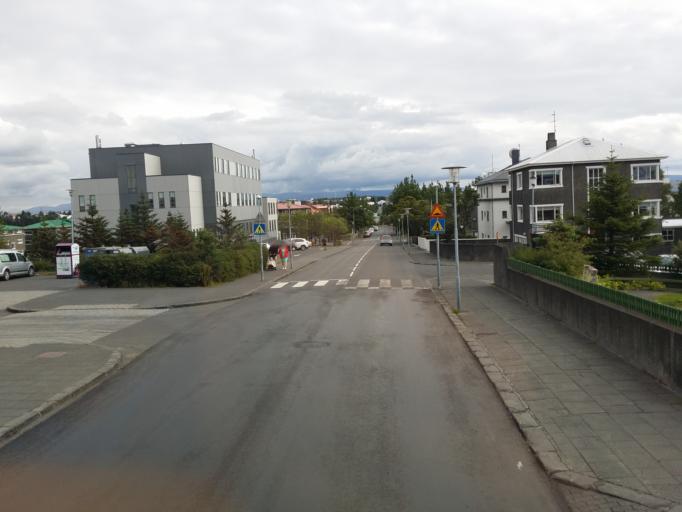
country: IS
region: Capital Region
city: Kopavogur
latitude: 64.1412
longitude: -21.9276
